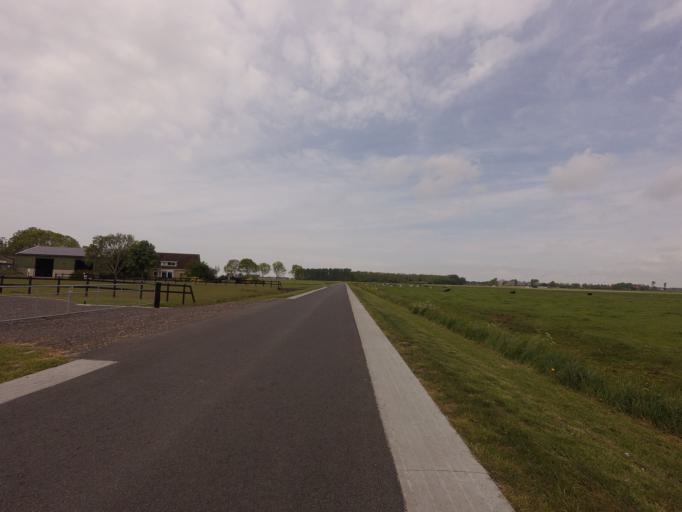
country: NL
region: Friesland
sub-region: Sudwest Fryslan
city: Bolsward
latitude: 53.0898
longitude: 5.4809
